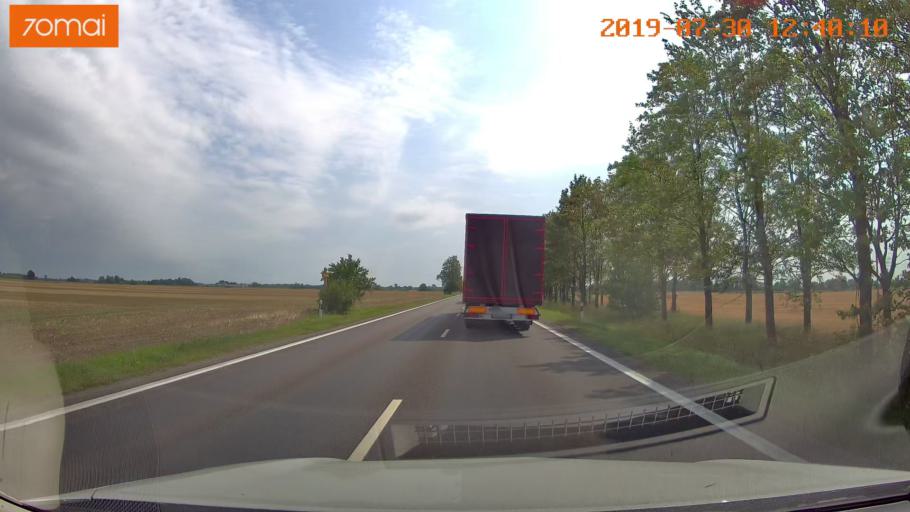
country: LT
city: Vilkaviskis
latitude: 54.6066
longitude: 23.1807
